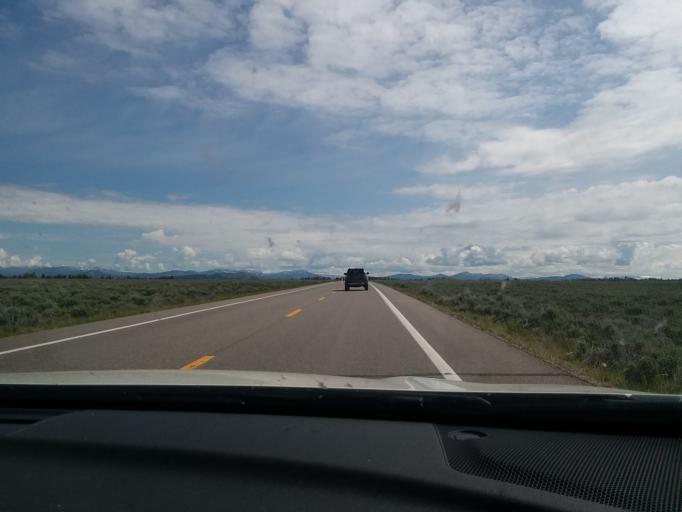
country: US
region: Wyoming
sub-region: Teton County
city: Jackson
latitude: 43.7352
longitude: -110.6413
